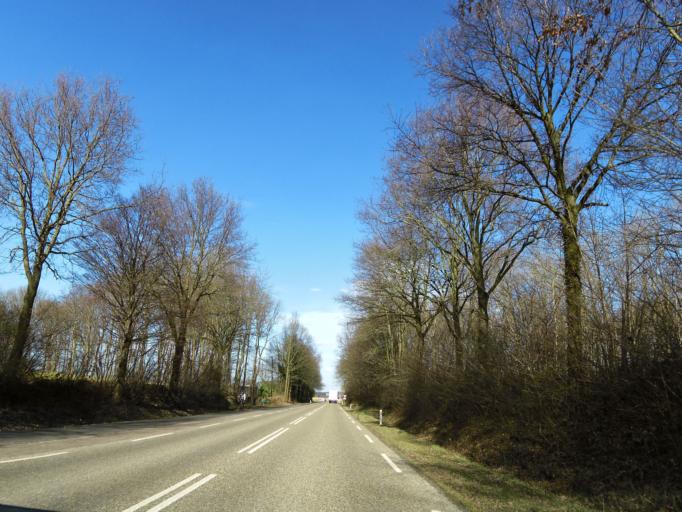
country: NL
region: Limburg
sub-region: Eijsden-Margraten
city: Margraten
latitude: 50.8128
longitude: 5.8440
